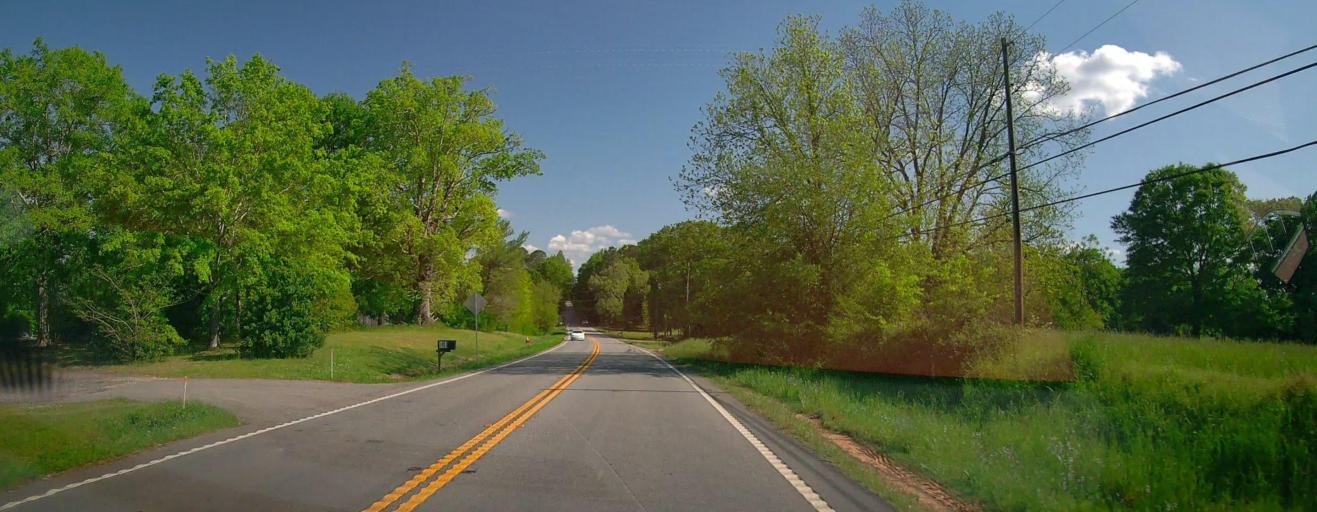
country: US
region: Georgia
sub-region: Morgan County
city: Madison
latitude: 33.6145
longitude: -83.4806
